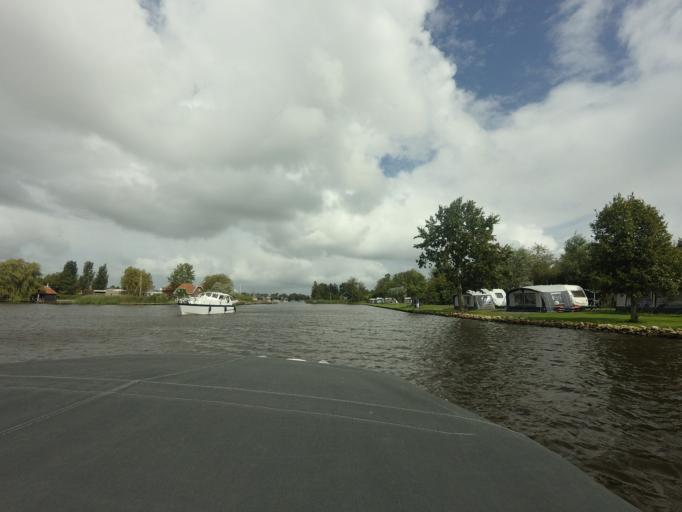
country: NL
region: Friesland
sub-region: Gemeente Boarnsterhim
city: Warten
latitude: 53.1275
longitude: 5.9373
